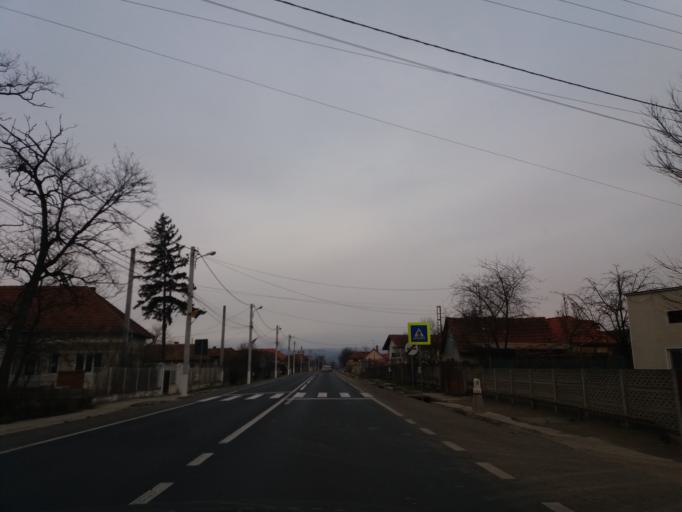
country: RO
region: Hunedoara
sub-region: Comuna Bacia
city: Bacia
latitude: 45.8030
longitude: 23.0122
